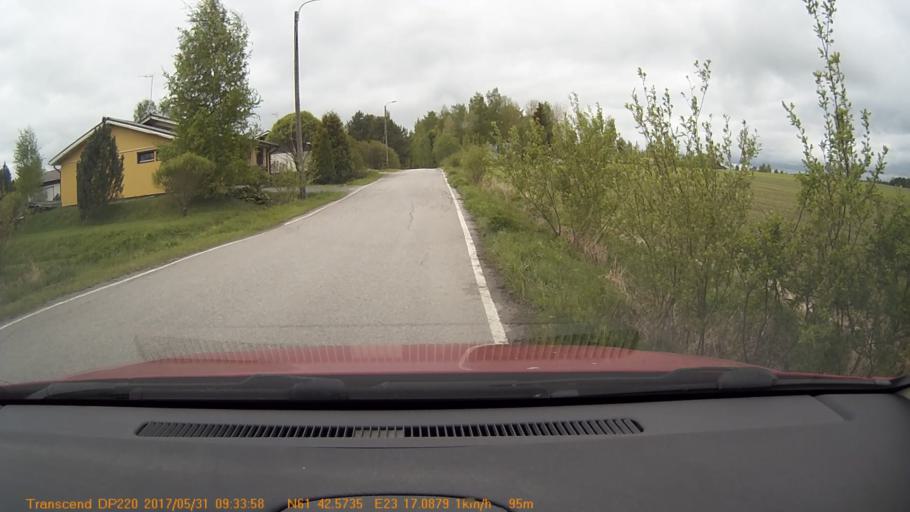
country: FI
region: Pirkanmaa
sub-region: Tampere
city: Viljakkala
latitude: 61.7096
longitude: 23.2847
